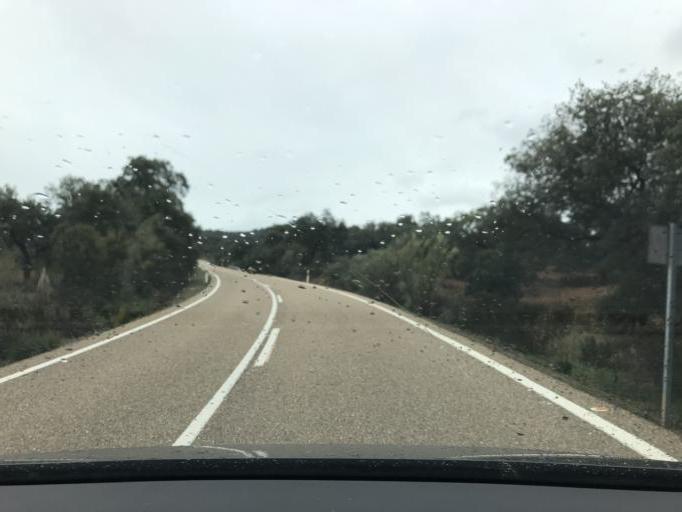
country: ES
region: Andalusia
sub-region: Province of Cordoba
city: Fuente Obejuna
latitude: 38.1759
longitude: -5.5067
